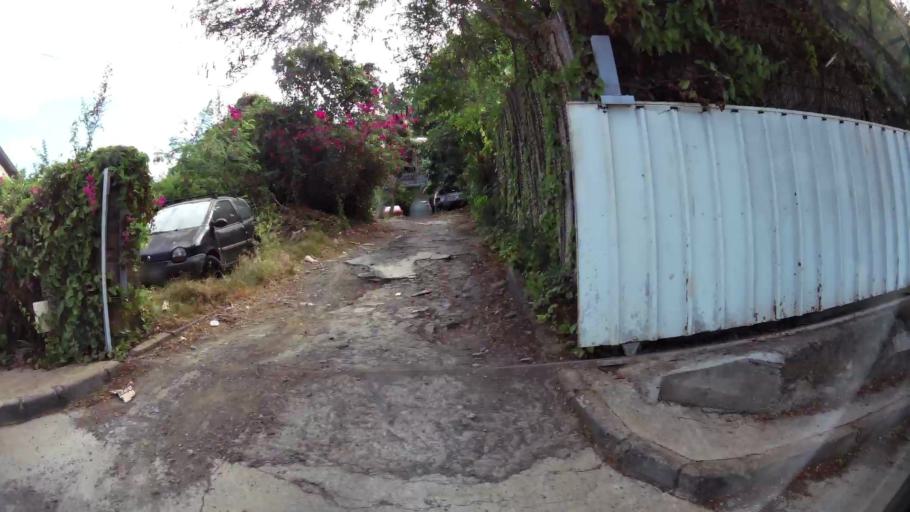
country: YT
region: Mamoudzou
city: Mamoudzou
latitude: -12.7819
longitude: 45.2195
